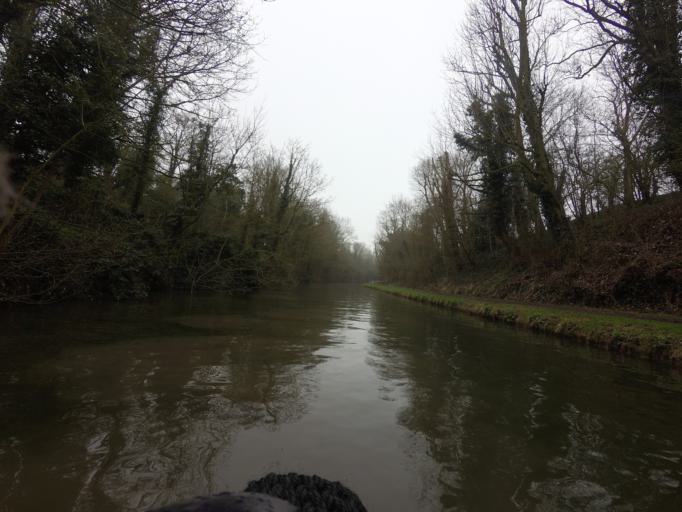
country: GB
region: England
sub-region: Hertfordshire
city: Tring
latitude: 51.8116
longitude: -0.6442
